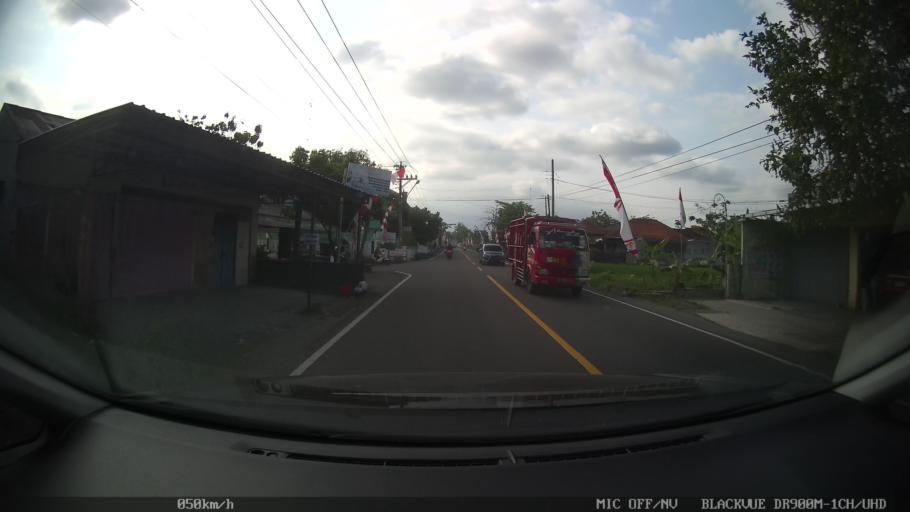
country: ID
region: Central Java
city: Candi Prambanan
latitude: -7.7004
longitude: 110.4660
